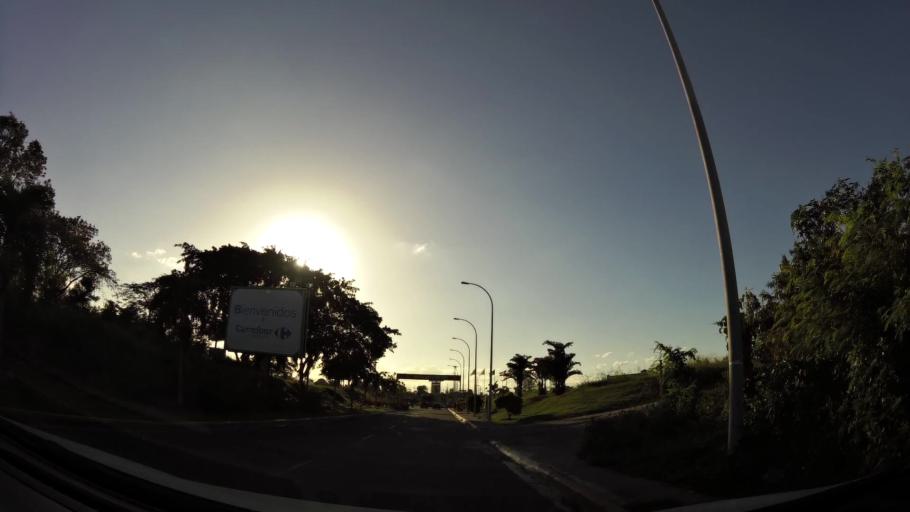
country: DO
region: Nacional
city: Santo Domingo
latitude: 18.4874
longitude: -69.9765
